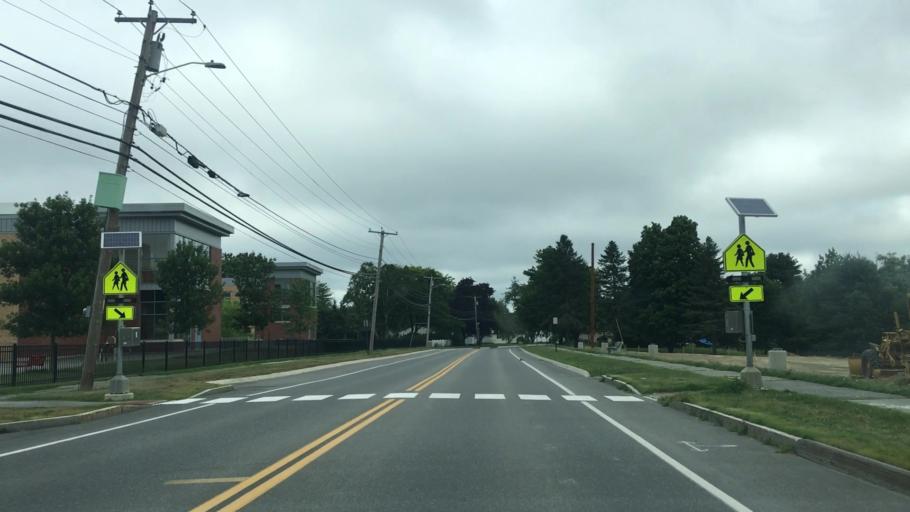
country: US
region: Maine
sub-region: Penobscot County
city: Brewer
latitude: 44.7758
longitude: -68.7694
